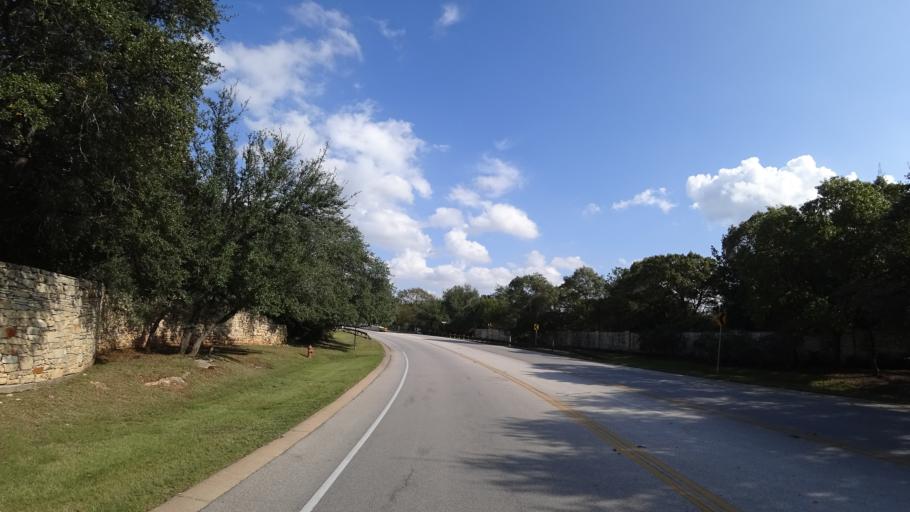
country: US
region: Texas
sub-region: Travis County
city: Lost Creek
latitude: 30.2962
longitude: -97.8535
